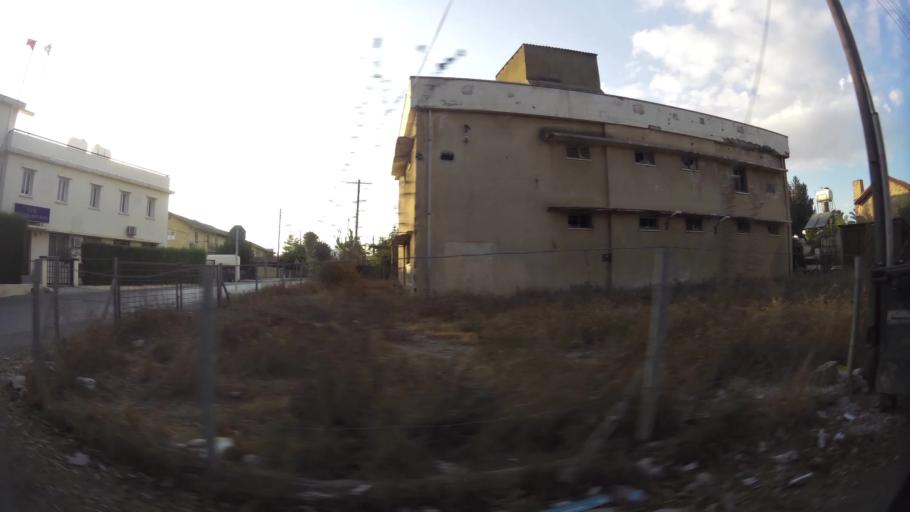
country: CY
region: Lefkosia
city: Nicosia
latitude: 35.1869
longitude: 33.3697
